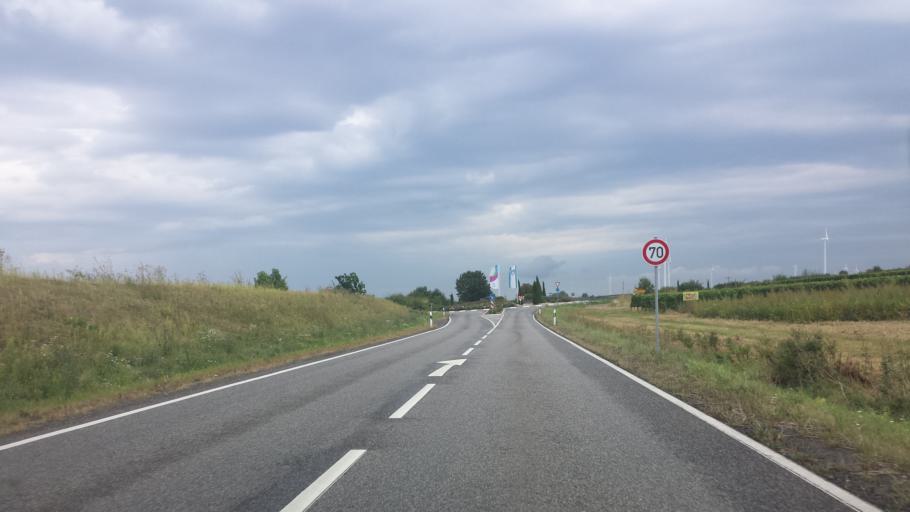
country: DE
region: Rheinland-Pfalz
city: Morstadt
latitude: 49.6578
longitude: 8.2515
